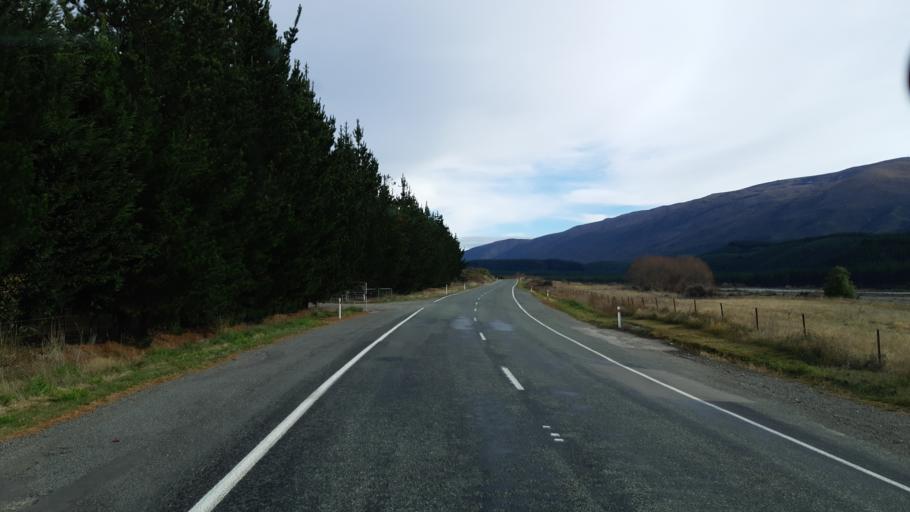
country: NZ
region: Tasman
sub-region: Tasman District
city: Wakefield
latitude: -41.6915
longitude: 173.1490
